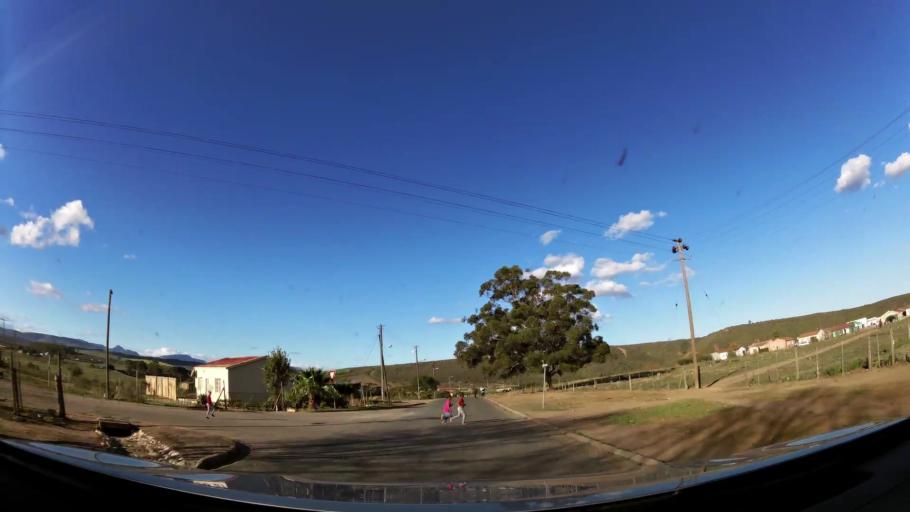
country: ZA
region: Western Cape
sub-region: Eden District Municipality
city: Riversdale
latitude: -34.1016
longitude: 20.9663
